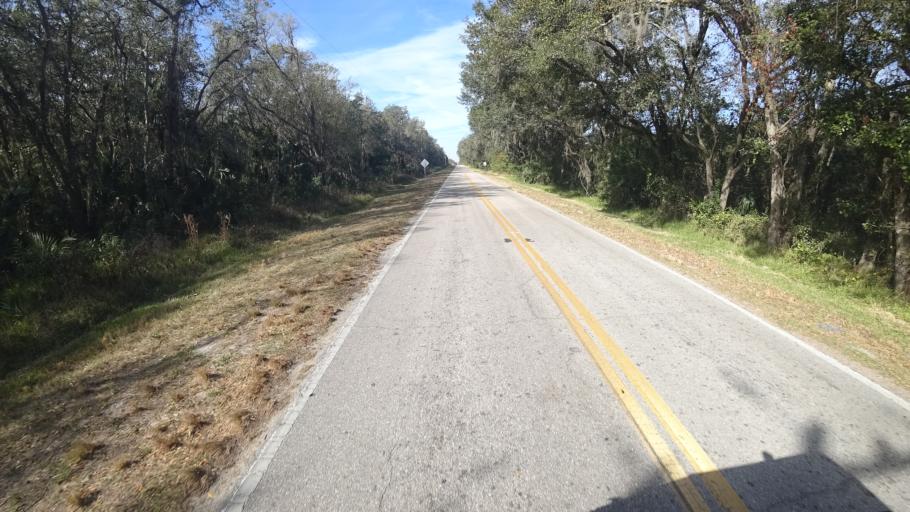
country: US
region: Florida
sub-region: Hillsborough County
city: Ruskin
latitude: 27.6305
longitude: -82.4002
